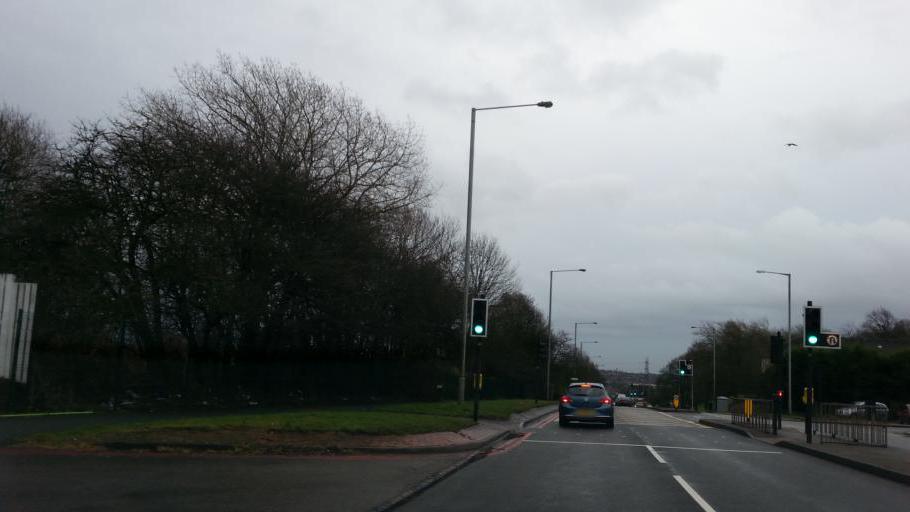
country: GB
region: England
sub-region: Sandwell
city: Oldbury
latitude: 52.5045
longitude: -2.0345
